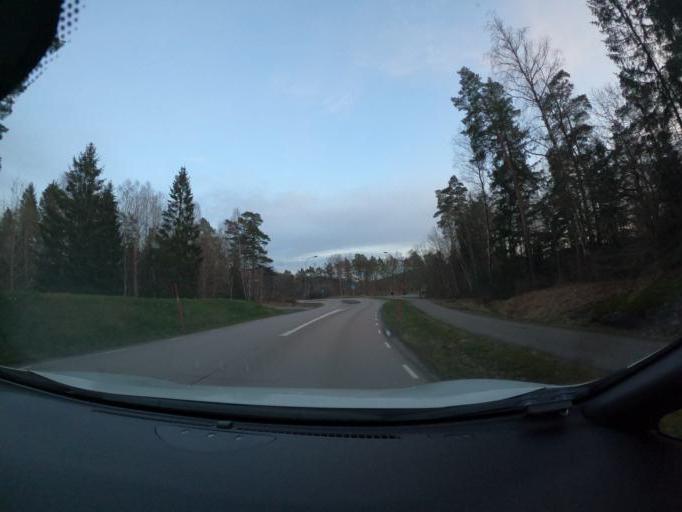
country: SE
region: Vaestra Goetaland
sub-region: Harryda Kommun
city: Molnlycke
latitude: 57.6505
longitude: 12.1416
